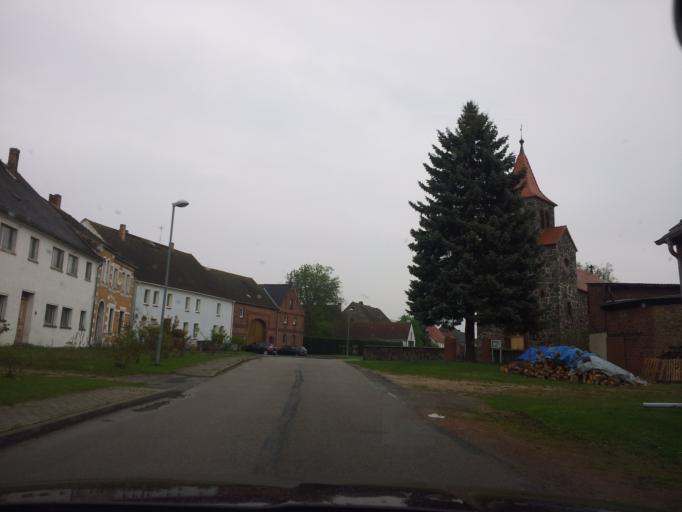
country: DE
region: Saxony-Anhalt
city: Zahna
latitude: 51.9779
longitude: 12.8293
